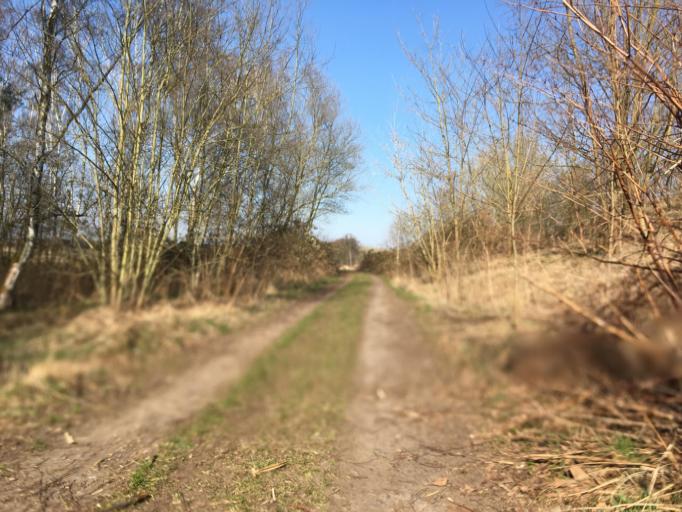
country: DE
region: Berlin
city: Buch
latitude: 52.6652
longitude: 13.4491
